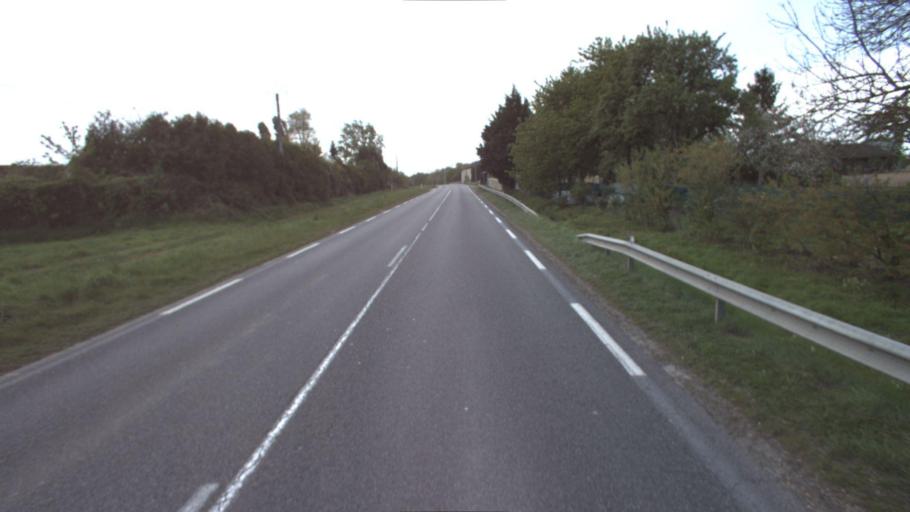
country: FR
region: Ile-de-France
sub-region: Departement de Seine-et-Marne
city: Jouy-le-Chatel
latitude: 48.6927
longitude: 3.1731
